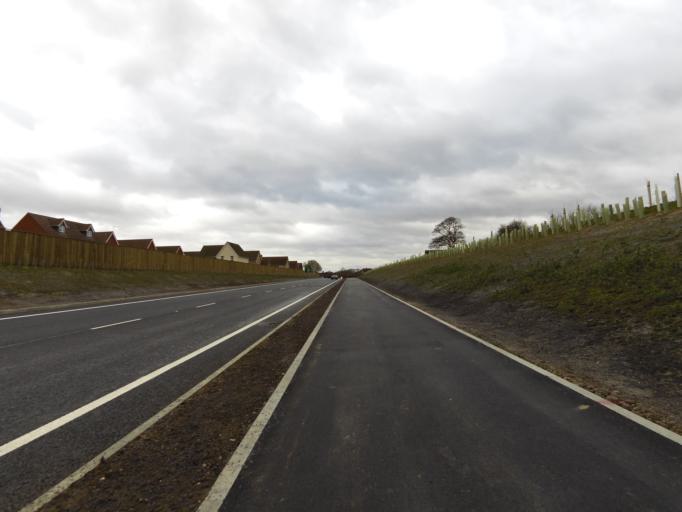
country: GB
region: England
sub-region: Norfolk
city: Hopton on Sea
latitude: 52.5013
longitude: 1.7273
